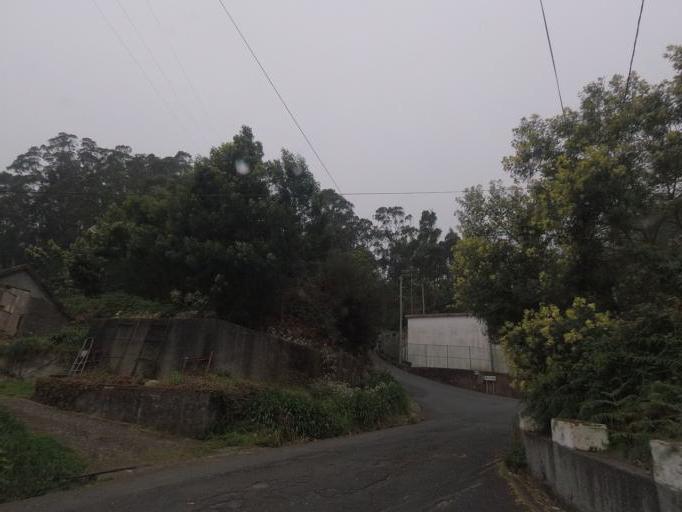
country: PT
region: Madeira
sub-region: Santa Cruz
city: Santa Cruz
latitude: 32.7317
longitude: -16.8227
